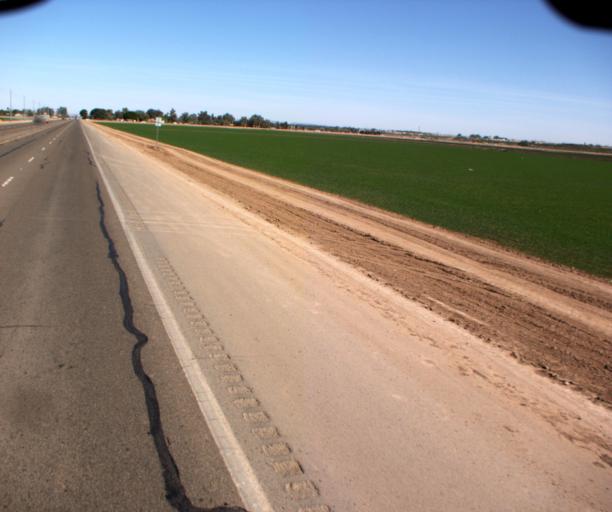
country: US
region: Arizona
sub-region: Yuma County
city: Somerton
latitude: 32.6271
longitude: -114.6498
